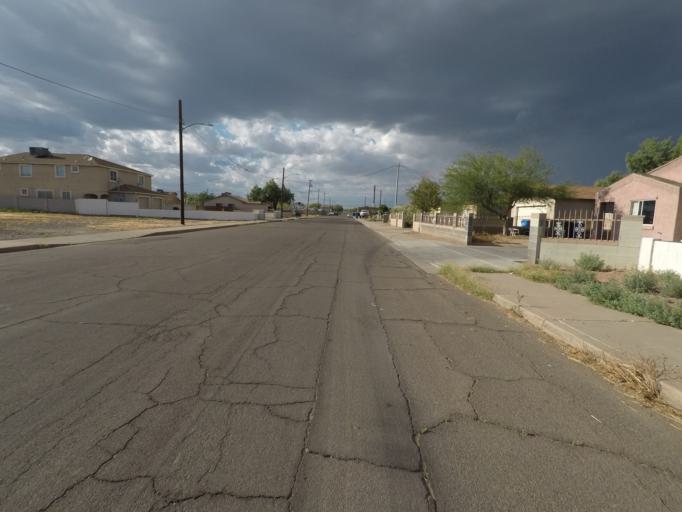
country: US
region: Arizona
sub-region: Maricopa County
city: Phoenix
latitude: 33.4351
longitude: -112.0890
